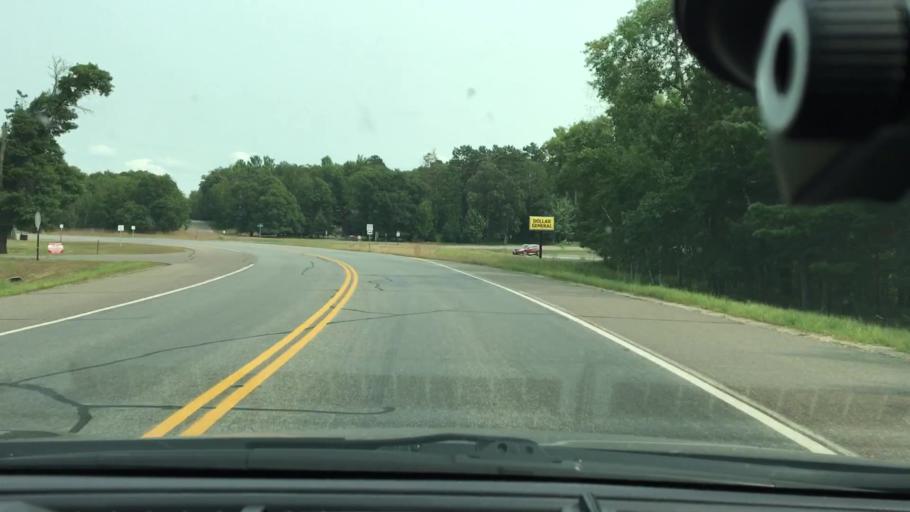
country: US
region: Minnesota
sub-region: Crow Wing County
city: Cross Lake
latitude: 46.6683
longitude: -94.1058
